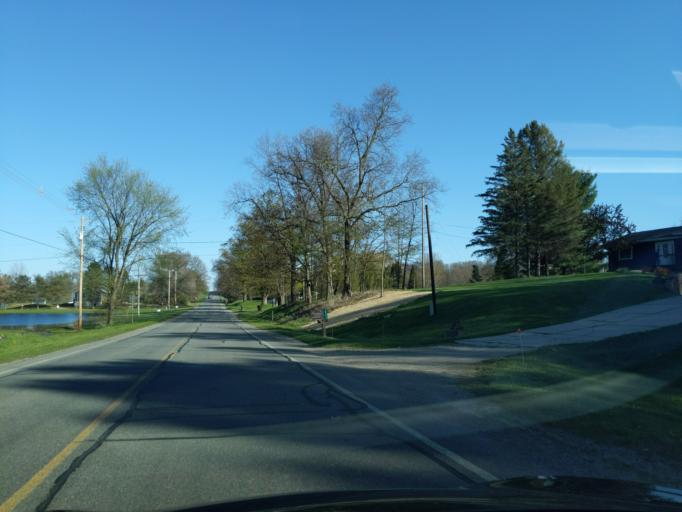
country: US
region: Michigan
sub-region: Ionia County
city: Portland
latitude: 42.8406
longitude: -84.8638
